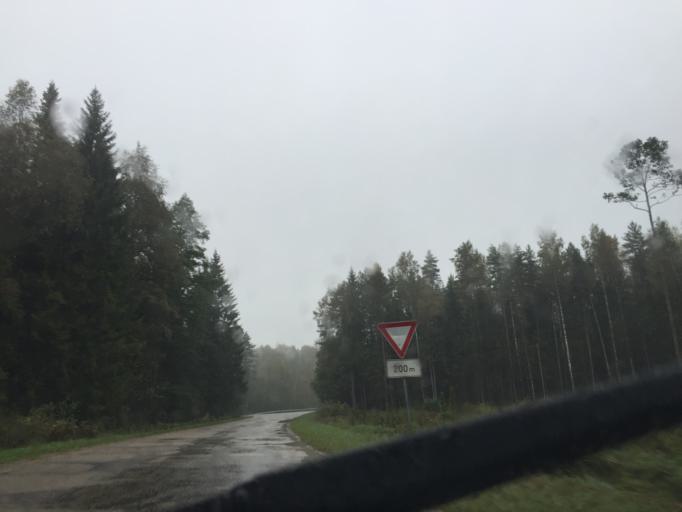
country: LV
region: Ropazu
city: Ropazi
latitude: 57.0094
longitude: 24.6810
